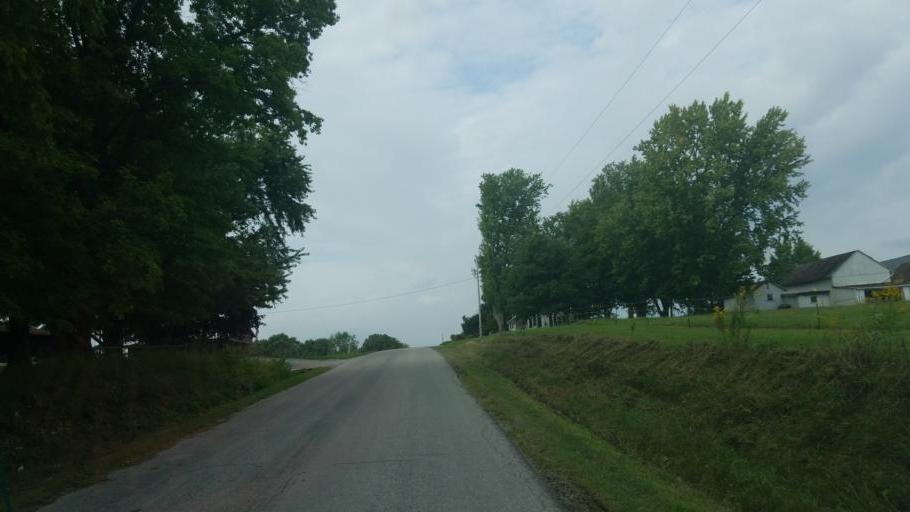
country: US
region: Ohio
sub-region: Wayne County
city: West Salem
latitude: 40.9631
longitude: -82.0538
